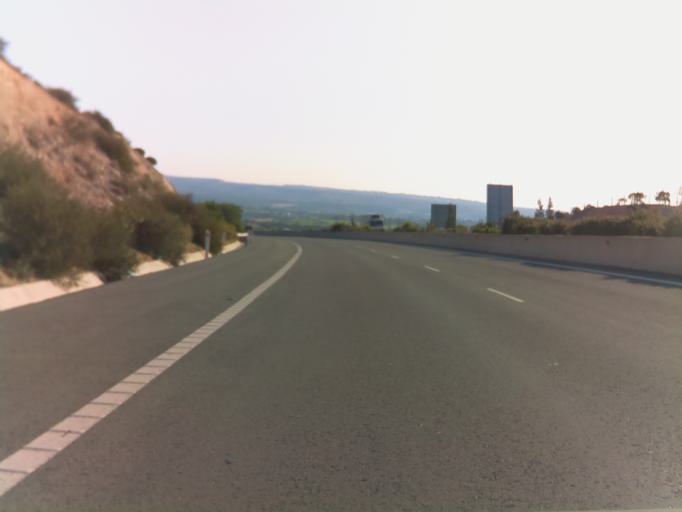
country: CY
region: Limassol
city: Pissouri
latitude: 34.6832
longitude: 32.7231
